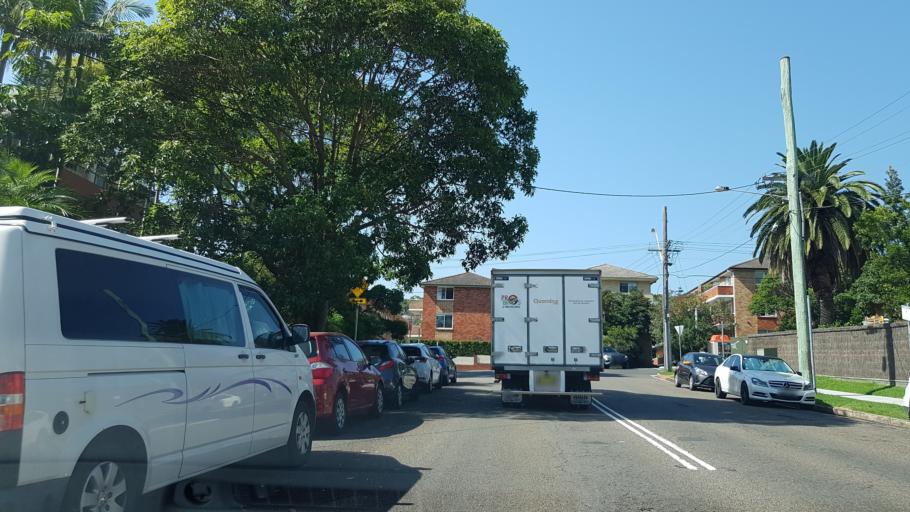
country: AU
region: New South Wales
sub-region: Warringah
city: North Curl Curl
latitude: -33.7548
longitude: 151.2919
